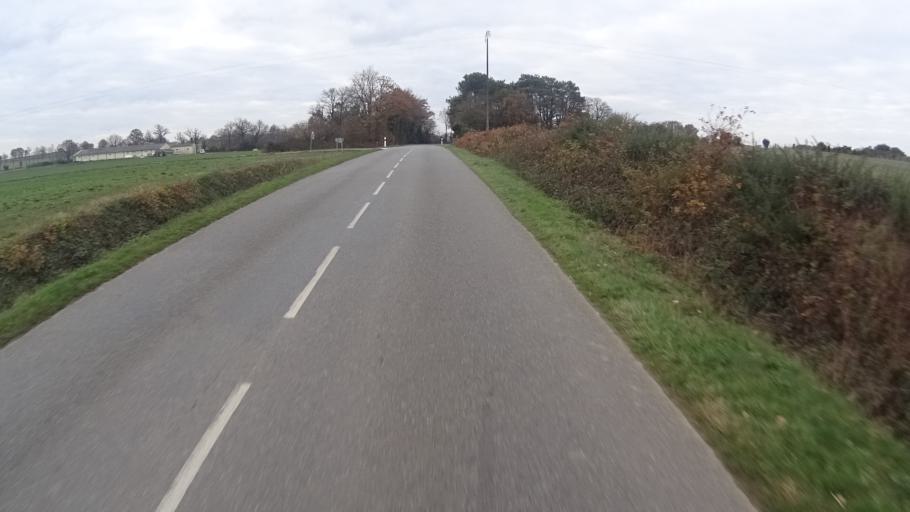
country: FR
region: Pays de la Loire
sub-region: Departement de la Loire-Atlantique
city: Avessac
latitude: 47.6615
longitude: -1.9391
